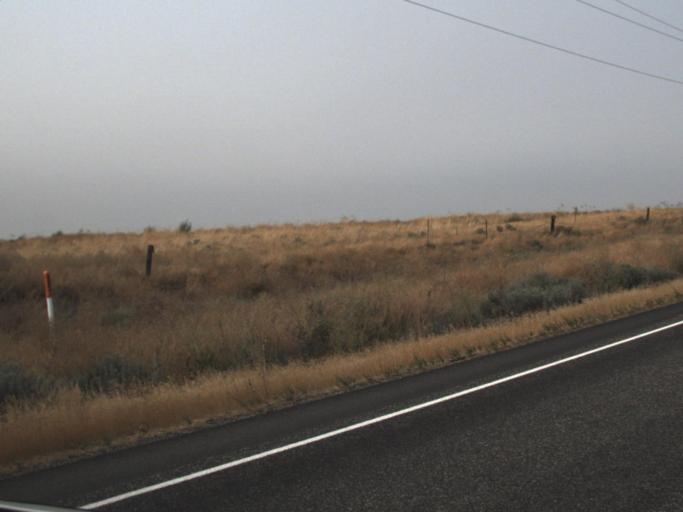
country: US
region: Oregon
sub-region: Morrow County
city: Irrigon
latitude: 46.0006
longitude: -119.6028
